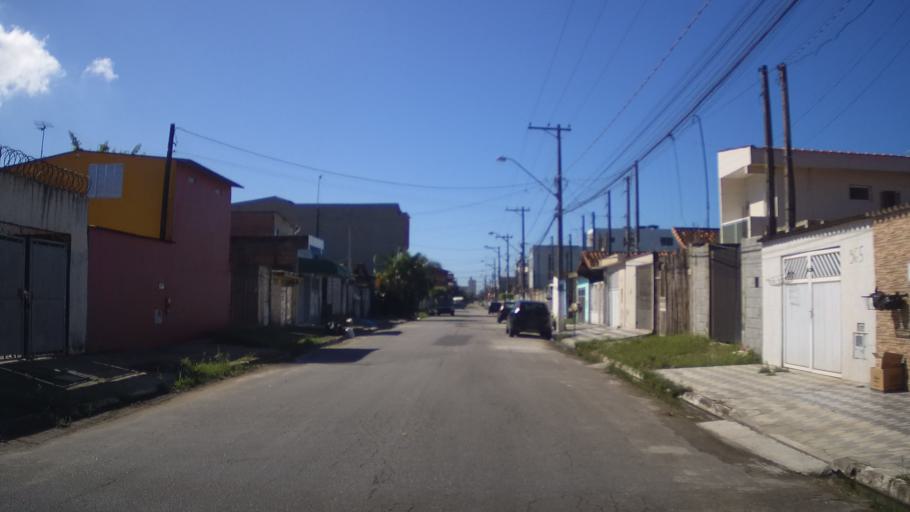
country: BR
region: Sao Paulo
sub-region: Praia Grande
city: Praia Grande
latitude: -24.0277
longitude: -46.5185
